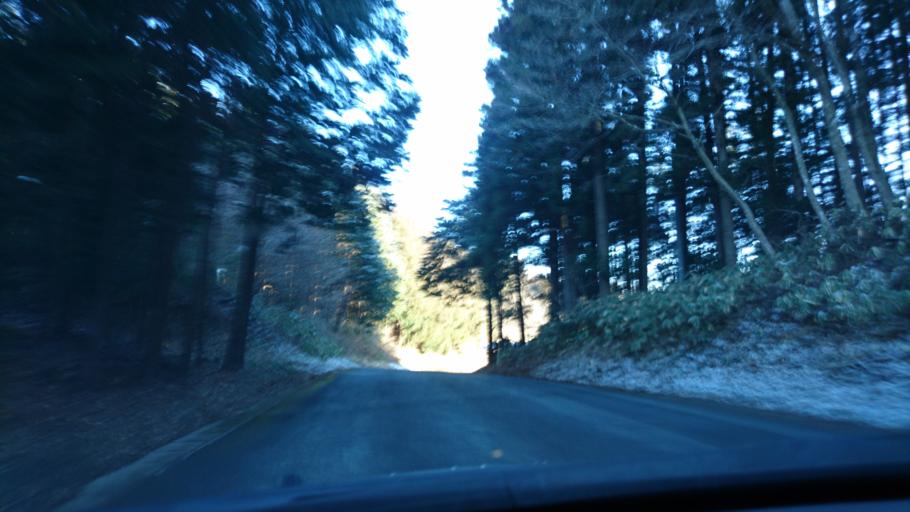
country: JP
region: Iwate
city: Ichinoseki
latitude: 38.8776
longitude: 141.3178
